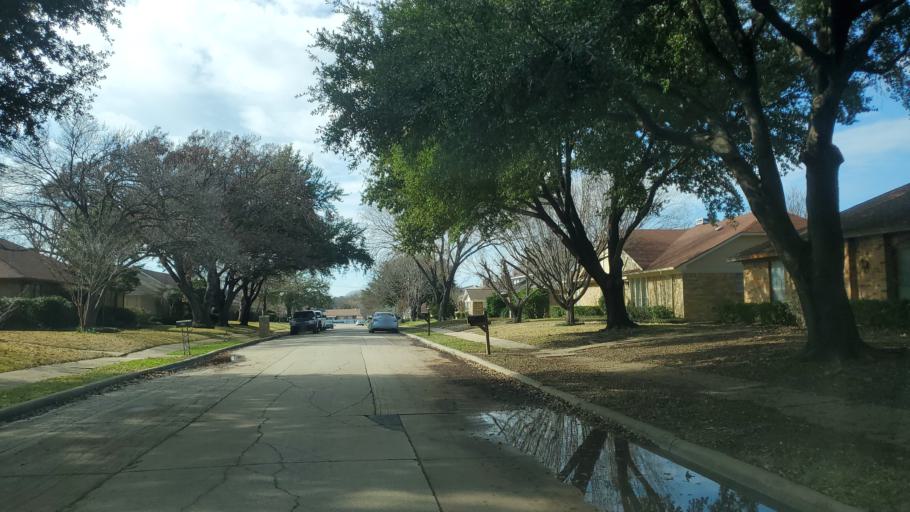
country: US
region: Texas
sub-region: Dallas County
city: Carrollton
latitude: 32.9795
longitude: -96.8818
